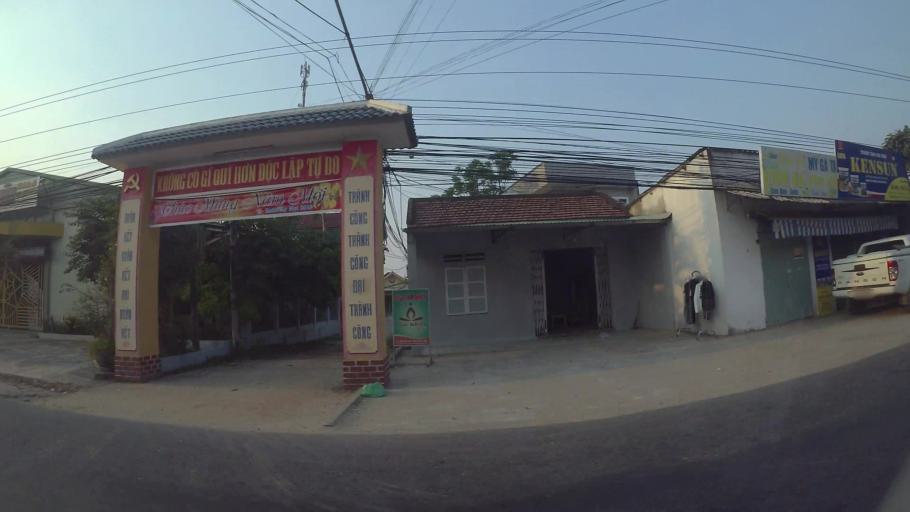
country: VN
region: Da Nang
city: Ngu Hanh Son
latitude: 15.9560
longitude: 108.2531
